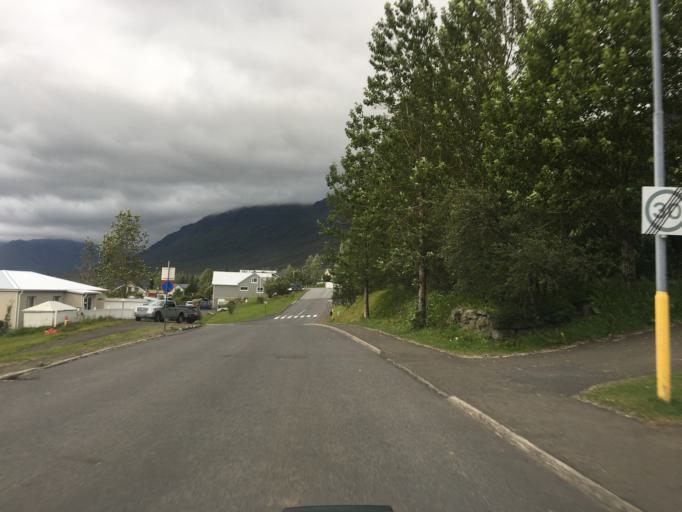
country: IS
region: East
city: Neskaupstadur
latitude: 65.1492
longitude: -13.6817
